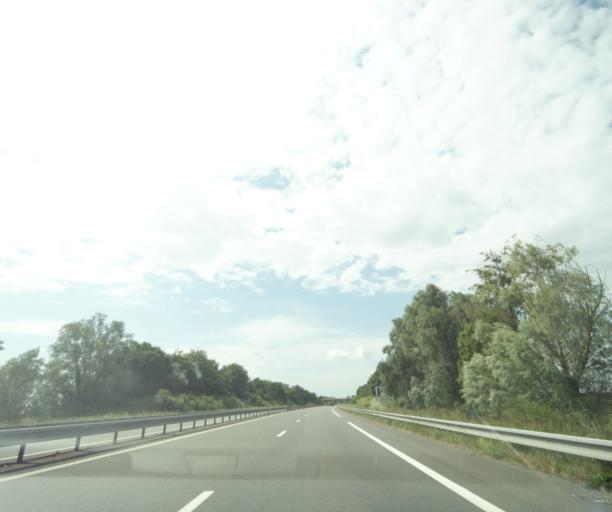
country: FR
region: Pays de la Loire
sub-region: Departement de Maine-et-Loire
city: Jumelles
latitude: 47.3902
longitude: -0.1035
